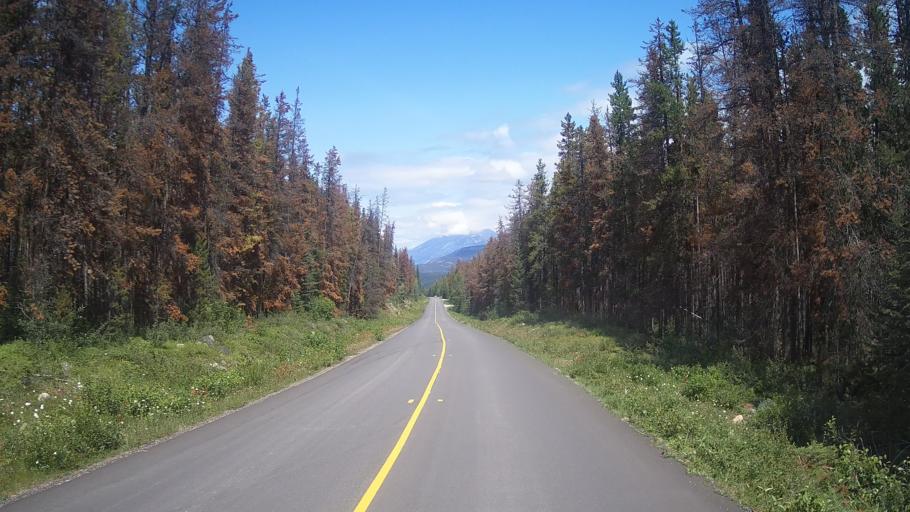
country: CA
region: Alberta
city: Jasper Park Lodge
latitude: 52.7771
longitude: -118.0326
